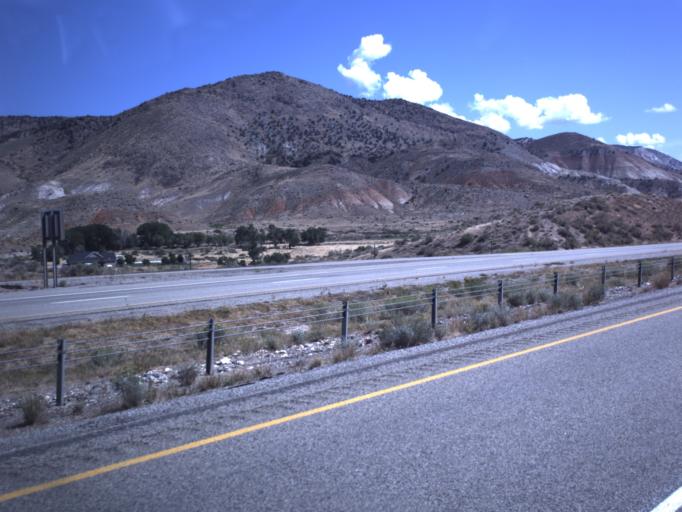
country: US
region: Utah
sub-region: Sevier County
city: Salina
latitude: 38.9331
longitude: -111.8491
